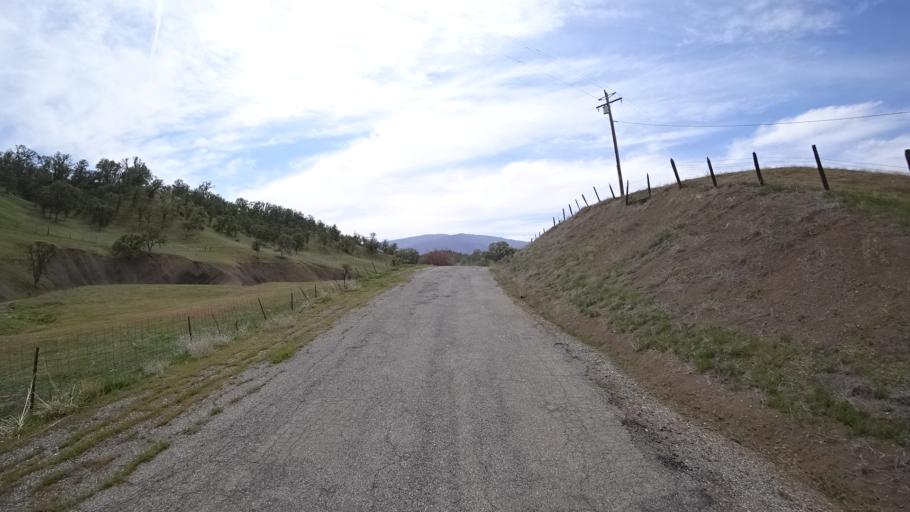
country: US
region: California
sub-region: Glenn County
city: Willows
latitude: 39.6135
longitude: -122.5733
